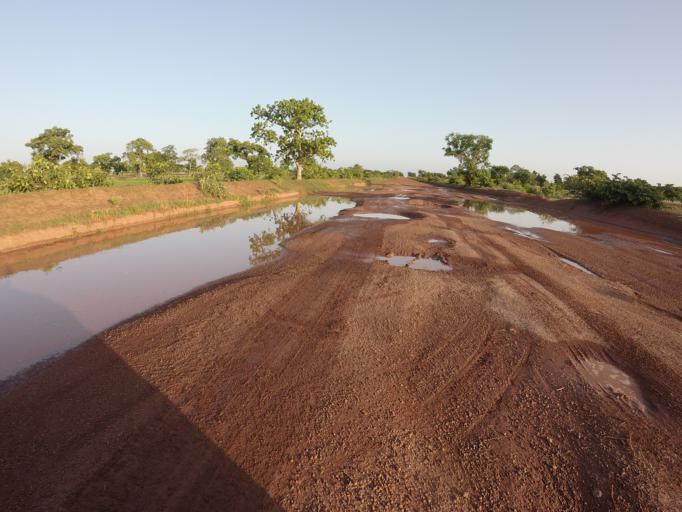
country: TG
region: Savanes
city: Sansanne-Mango
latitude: 10.2713
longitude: -0.0818
